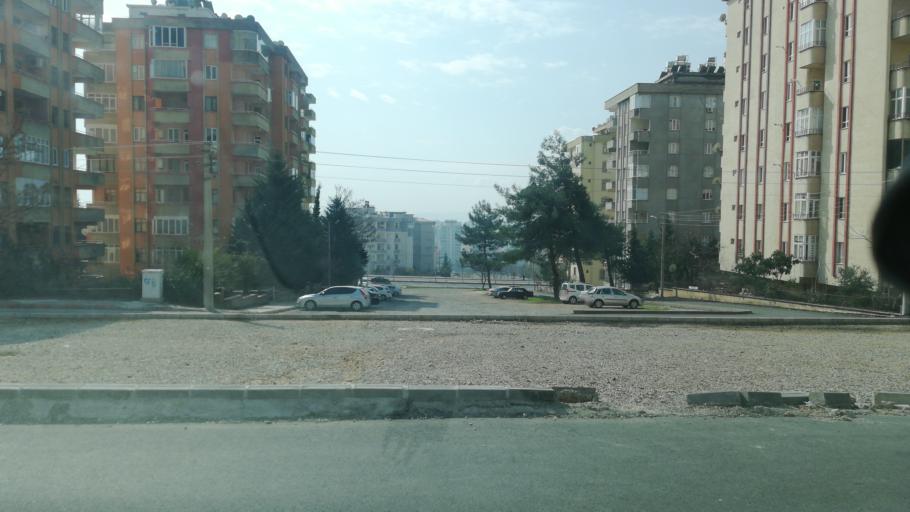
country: TR
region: Kahramanmaras
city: Kahramanmaras
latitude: 37.5880
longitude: 36.8830
